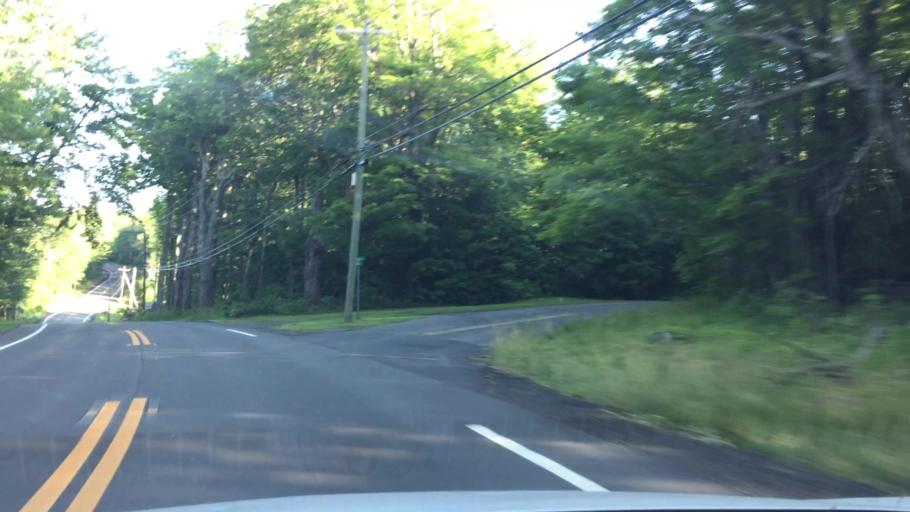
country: US
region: Massachusetts
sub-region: Berkshire County
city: Becket
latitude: 42.3053
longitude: -73.0645
